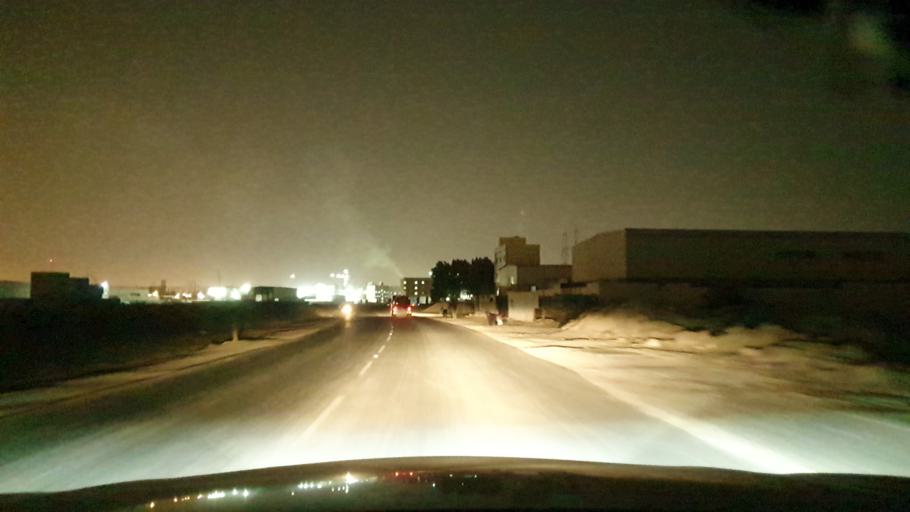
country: BH
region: Northern
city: Sitrah
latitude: 26.0912
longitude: 50.6158
